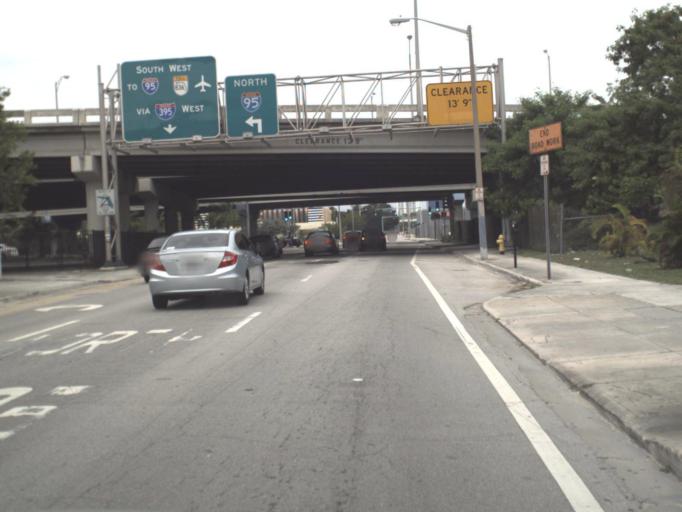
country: US
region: Florida
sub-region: Miami-Dade County
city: Miami
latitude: 25.7850
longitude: -80.1923
